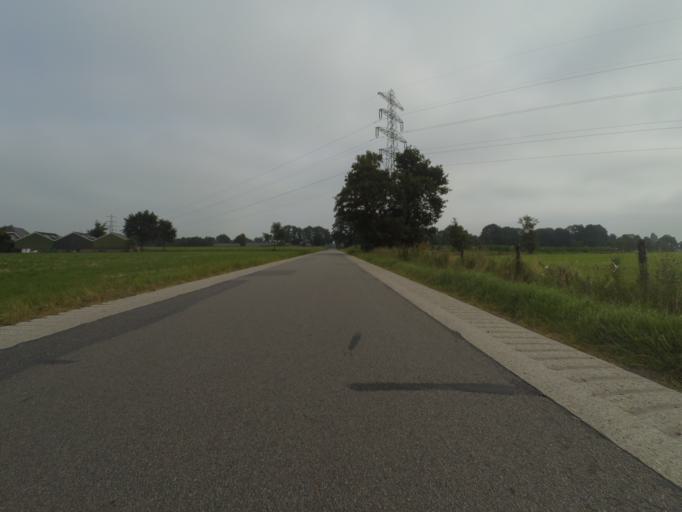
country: NL
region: Gelderland
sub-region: Gemeente Barneveld
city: Kootwijkerbroek
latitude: 52.1413
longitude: 5.6557
